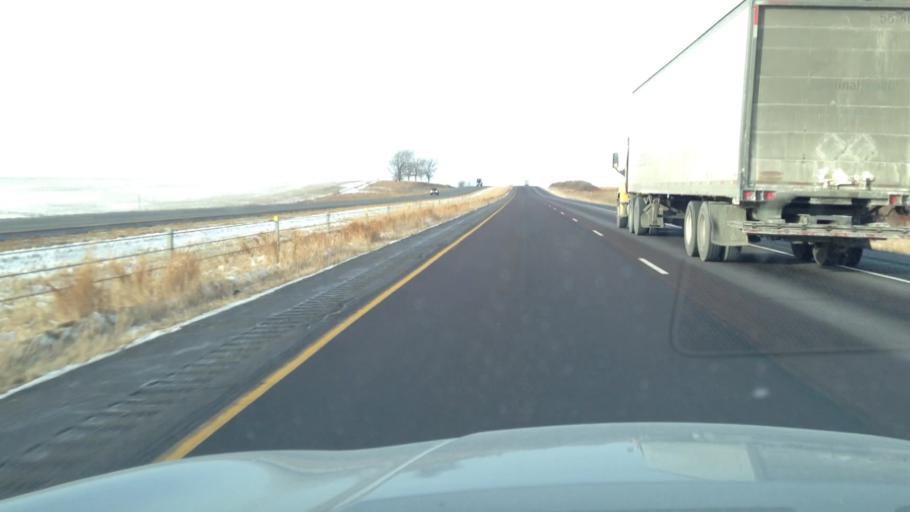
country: US
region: Iowa
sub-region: Poweshiek County
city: Grinnell
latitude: 41.6958
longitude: -92.6501
